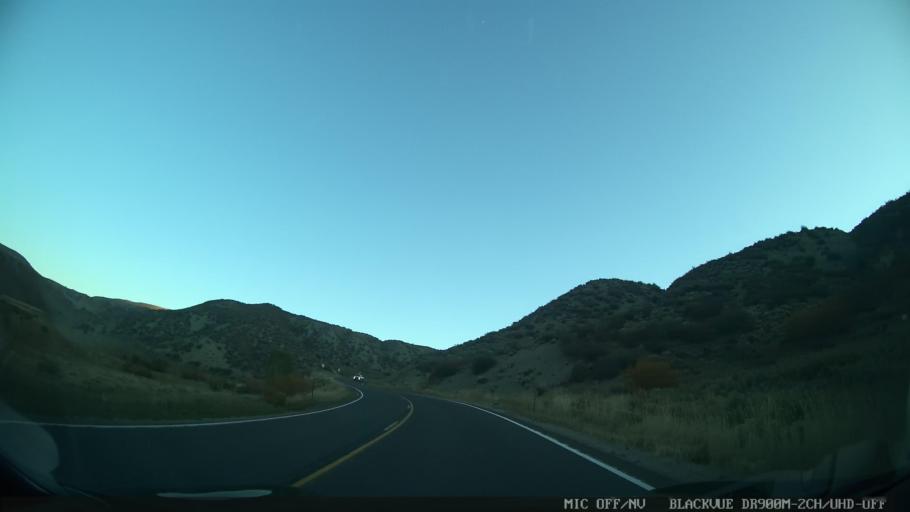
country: US
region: Colorado
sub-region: Eagle County
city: Edwards
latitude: 39.7964
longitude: -106.6797
